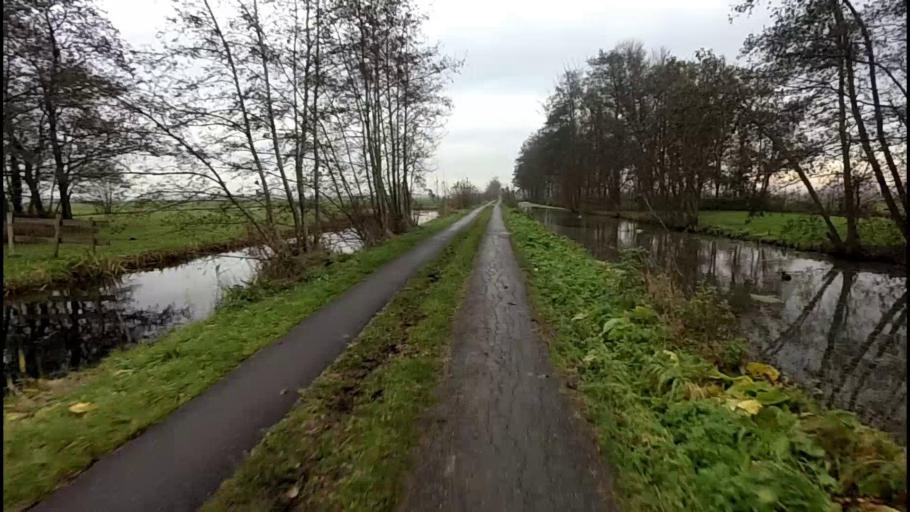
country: NL
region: South Holland
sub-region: Gemeente Gouda
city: Gouda
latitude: 51.9927
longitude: 4.7080
